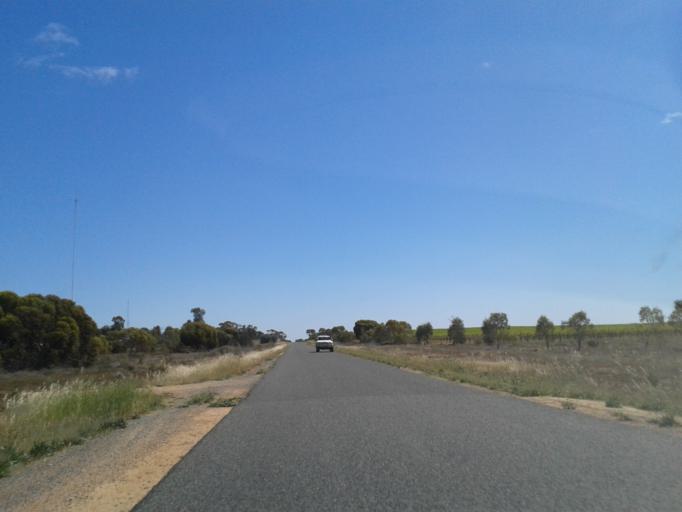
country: AU
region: New South Wales
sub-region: Wentworth
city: Dareton
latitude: -34.1959
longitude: 141.9970
